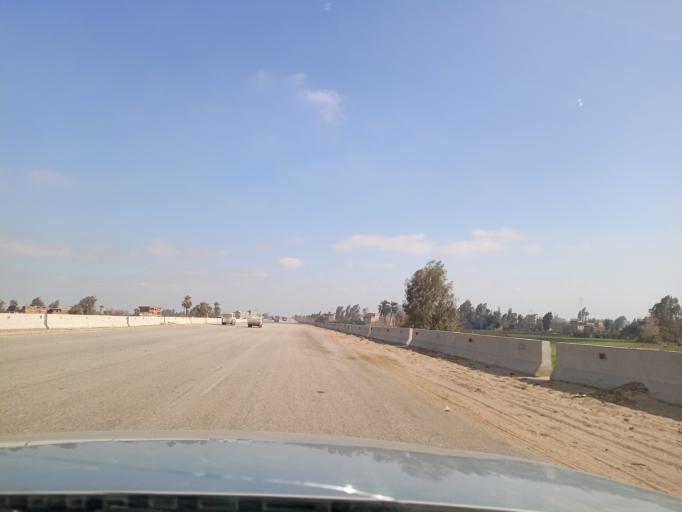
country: EG
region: Muhafazat al Minufiyah
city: Al Bajur
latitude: 30.4265
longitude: 31.0931
